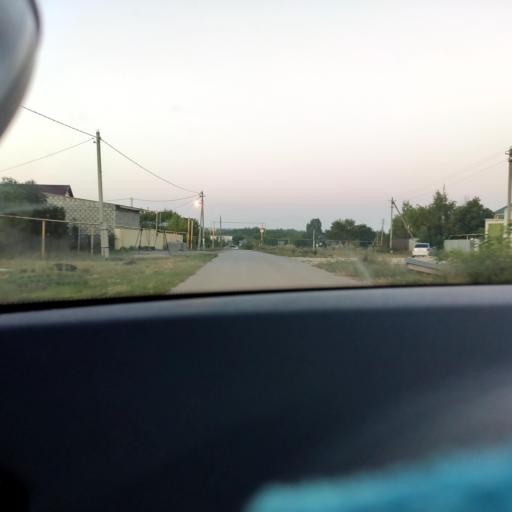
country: RU
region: Samara
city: Novokuybyshevsk
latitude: 53.0757
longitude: 50.0130
